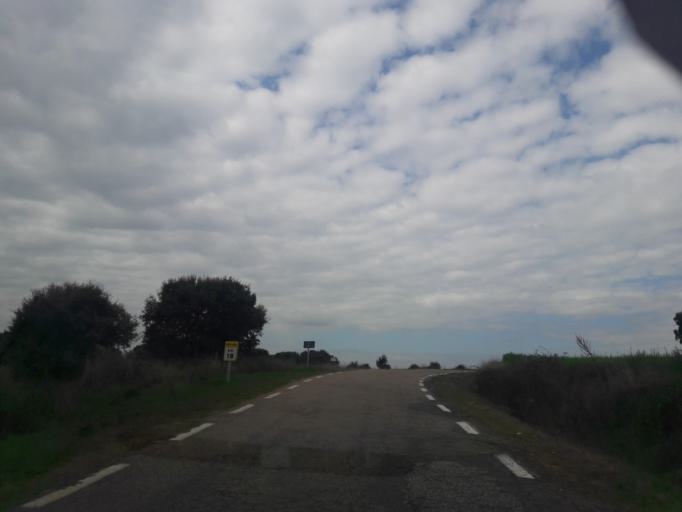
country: ES
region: Castille and Leon
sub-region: Provincia de Salamanca
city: Serradilla del Arroyo
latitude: 40.5222
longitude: -6.3759
